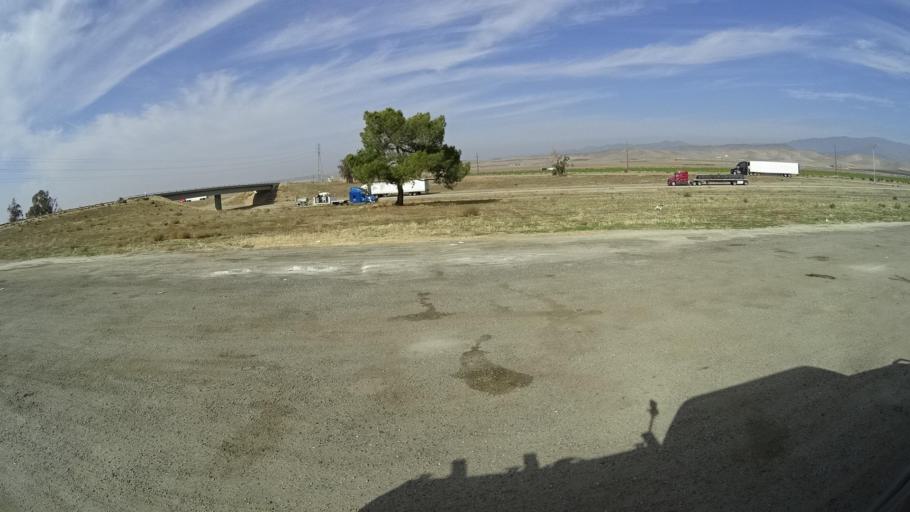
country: US
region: California
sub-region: Kern County
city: Arvin
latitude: 35.3285
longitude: -118.8067
